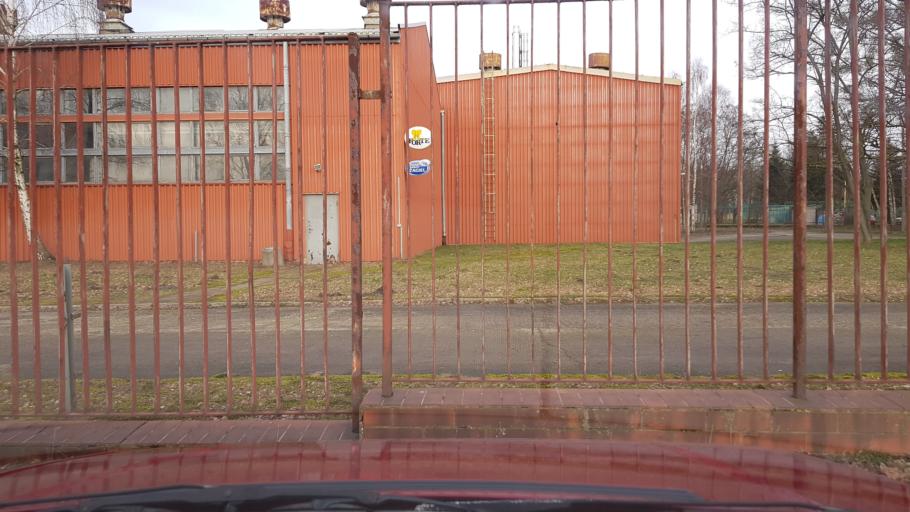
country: PL
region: West Pomeranian Voivodeship
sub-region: Powiat policki
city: Police
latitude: 53.5473
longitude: 14.5633
